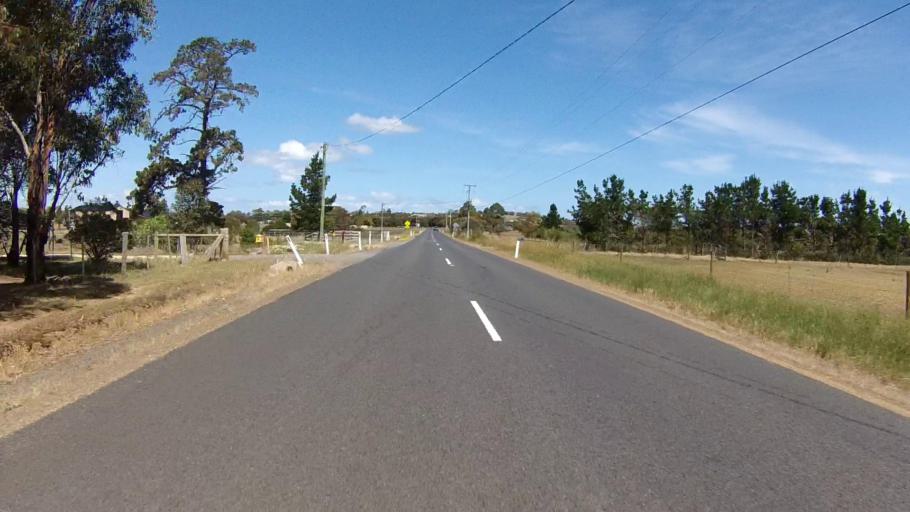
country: AU
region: Tasmania
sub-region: Sorell
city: Sorell
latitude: -42.7764
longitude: 147.5205
